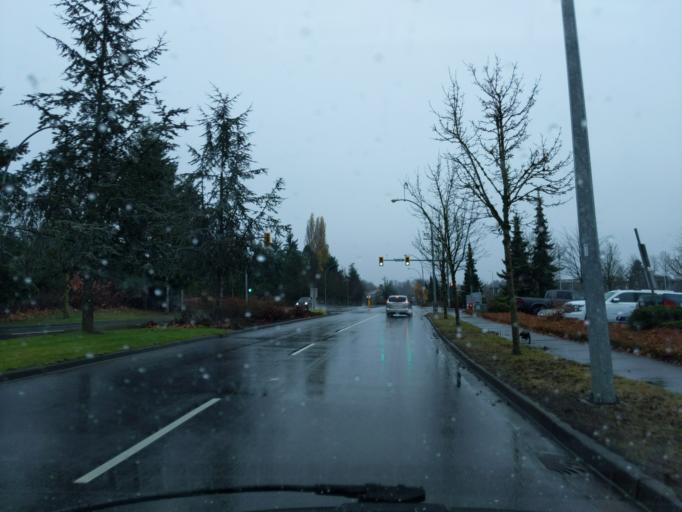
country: CA
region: British Columbia
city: Walnut Grove
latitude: 49.1693
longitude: -122.6627
